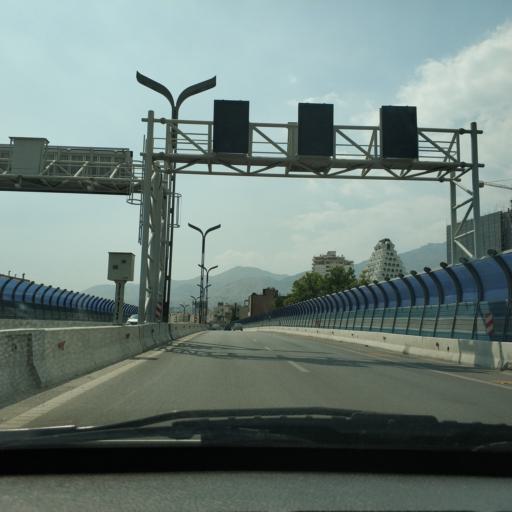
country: IR
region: Tehran
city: Tajrish
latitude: 35.7926
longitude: 51.4647
